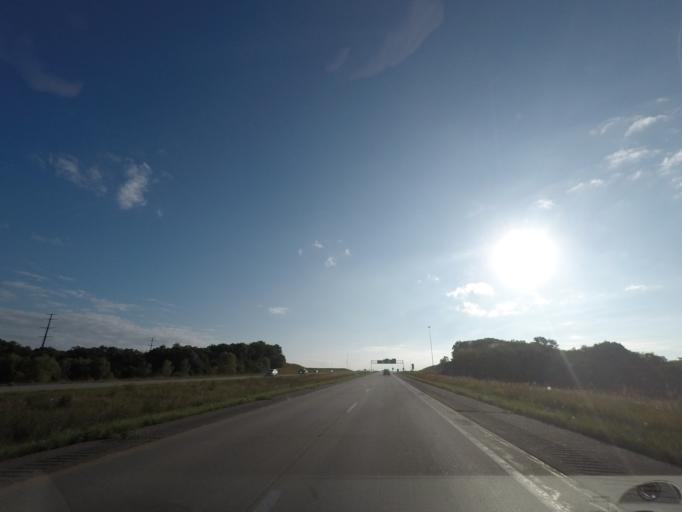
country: US
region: Iowa
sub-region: Warren County
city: Carlisle
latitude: 41.5044
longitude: -93.5826
